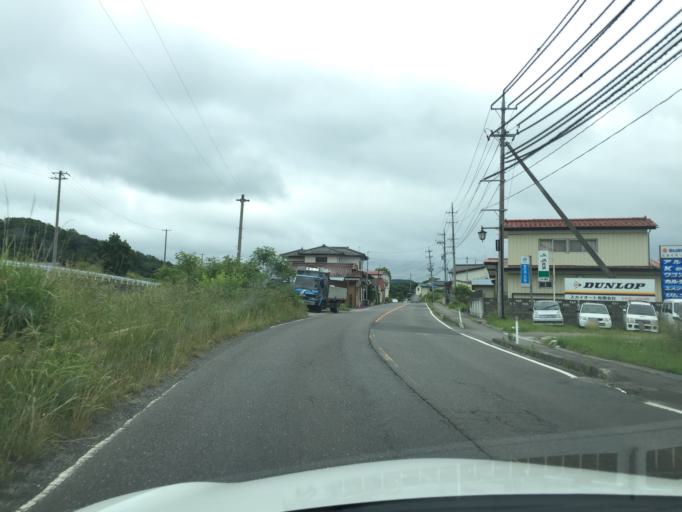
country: JP
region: Fukushima
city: Funehikimachi-funehiki
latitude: 37.4193
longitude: 140.6064
